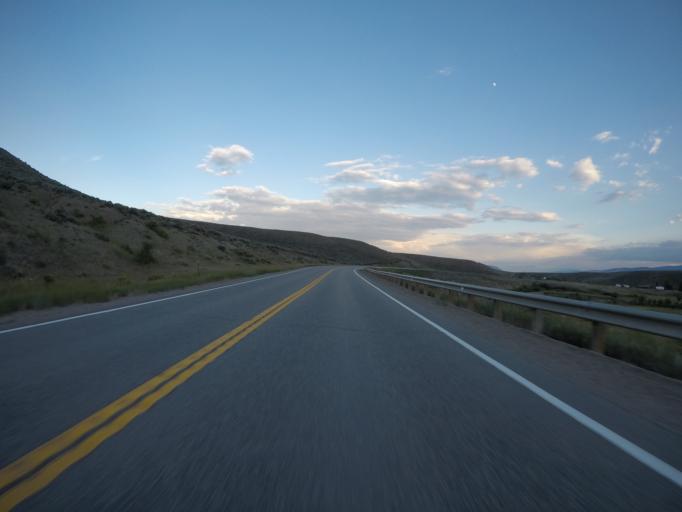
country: US
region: Colorado
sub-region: Grand County
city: Kremmling
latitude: 40.2551
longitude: -106.4528
